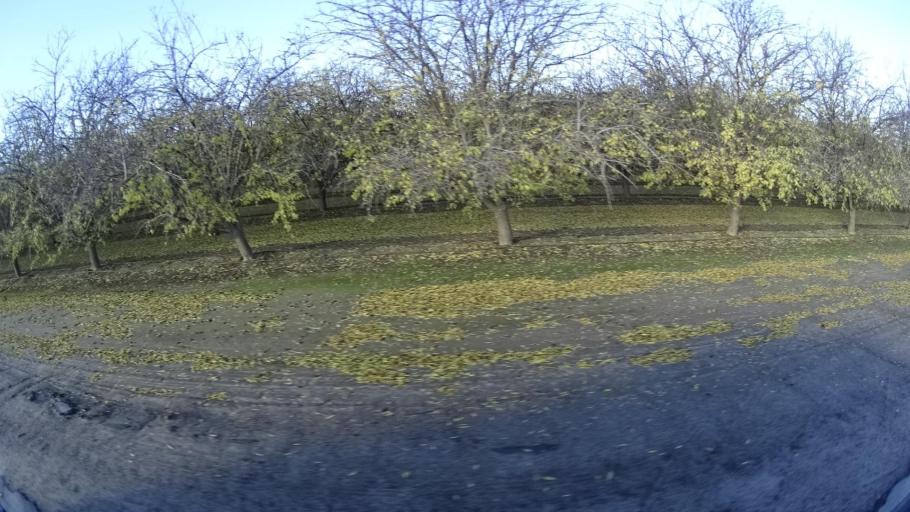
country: US
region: California
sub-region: Kern County
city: Delano
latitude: 35.7457
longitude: -119.3300
